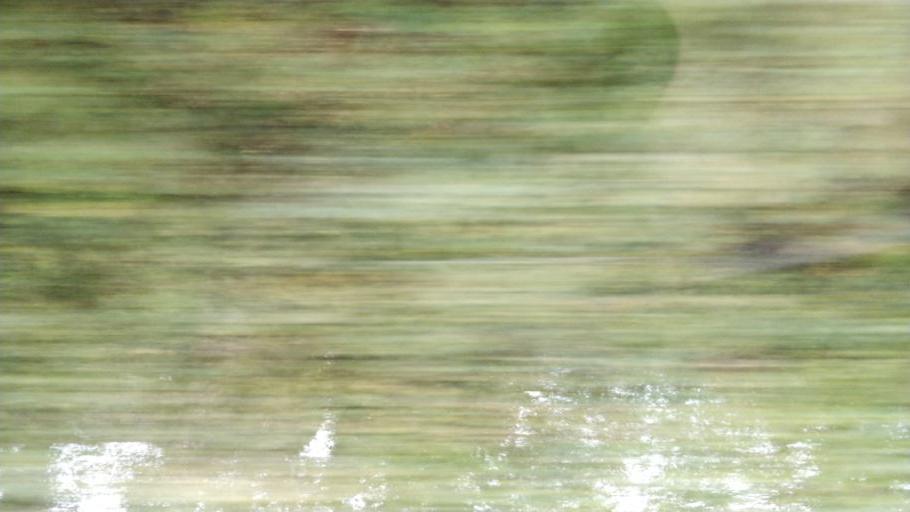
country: GB
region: England
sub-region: Borough of Wigan
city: Atherton
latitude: 53.5293
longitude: -2.4780
